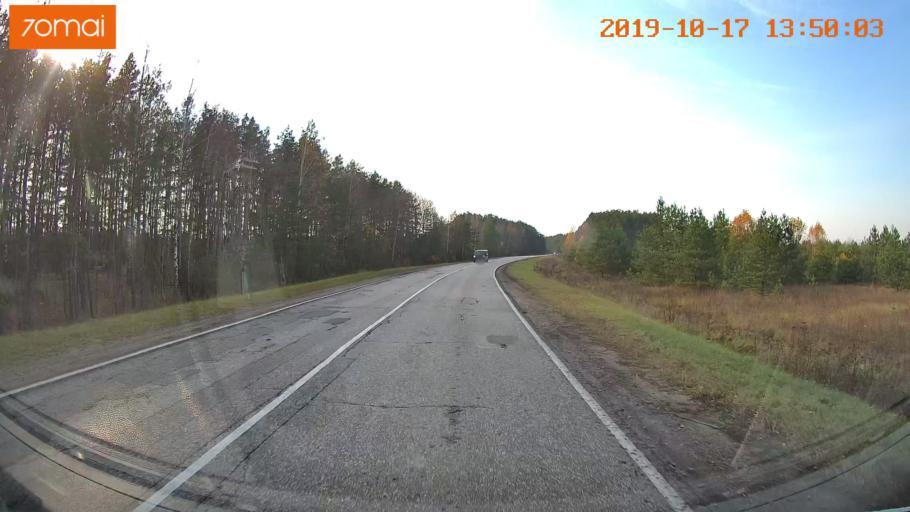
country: RU
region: Rjazan
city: Tuma
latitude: 55.1418
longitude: 40.4170
